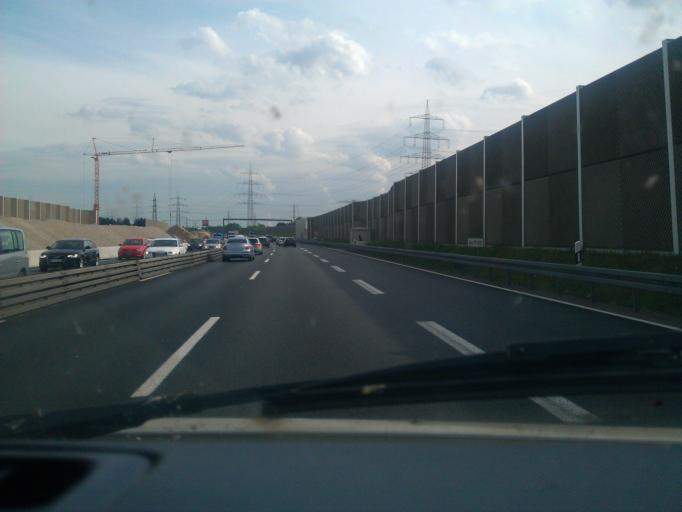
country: DE
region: North Rhine-Westphalia
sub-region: Regierungsbezirk Dusseldorf
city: Kaarst
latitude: 51.2281
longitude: 6.6383
